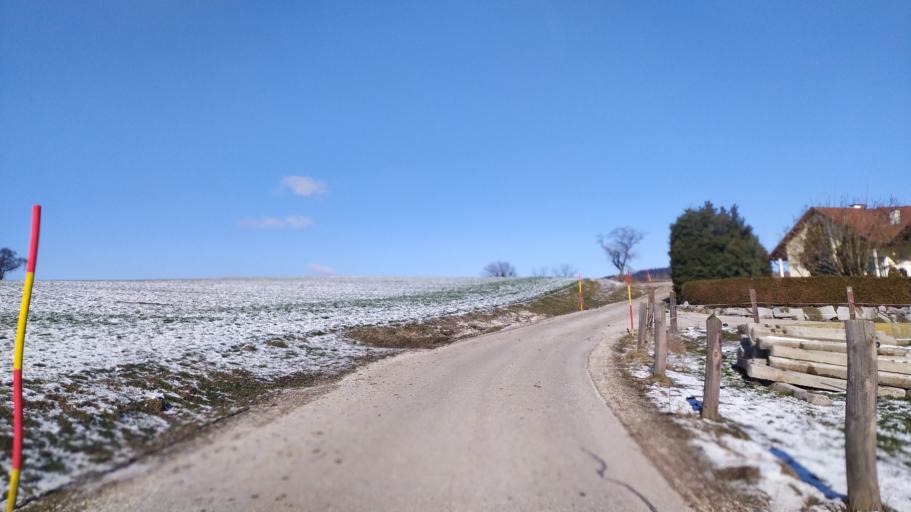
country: AT
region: Upper Austria
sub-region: Politischer Bezirk Urfahr-Umgebung
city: Ottensheim
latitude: 48.3206
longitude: 14.2169
